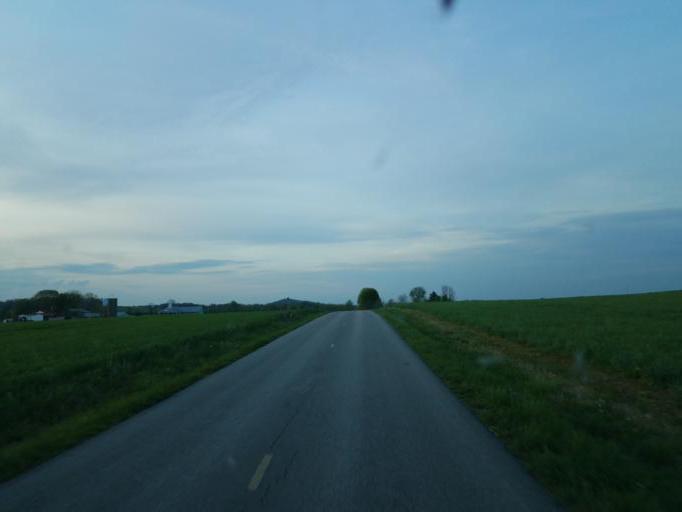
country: US
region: Kentucky
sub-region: Hart County
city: Munfordville
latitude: 37.2198
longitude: -85.6979
